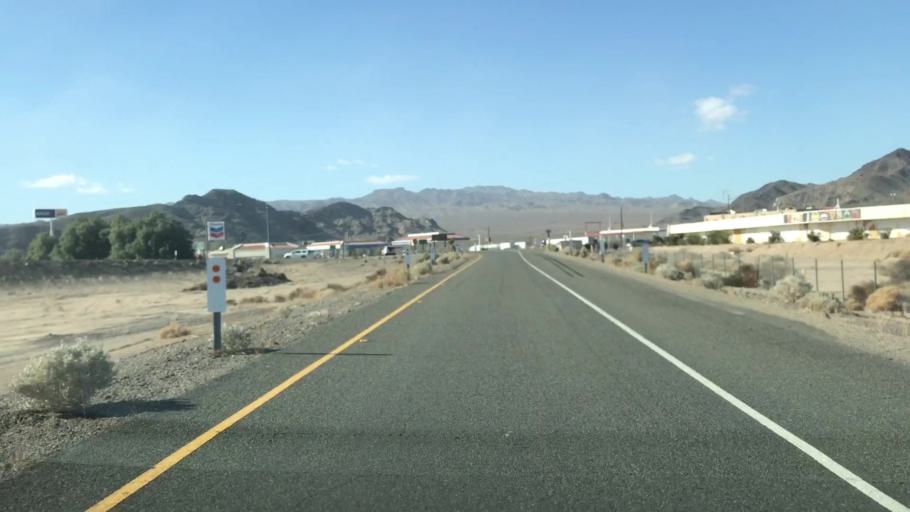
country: US
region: California
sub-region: San Bernardino County
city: Fort Irwin
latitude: 35.2647
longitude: -116.0728
